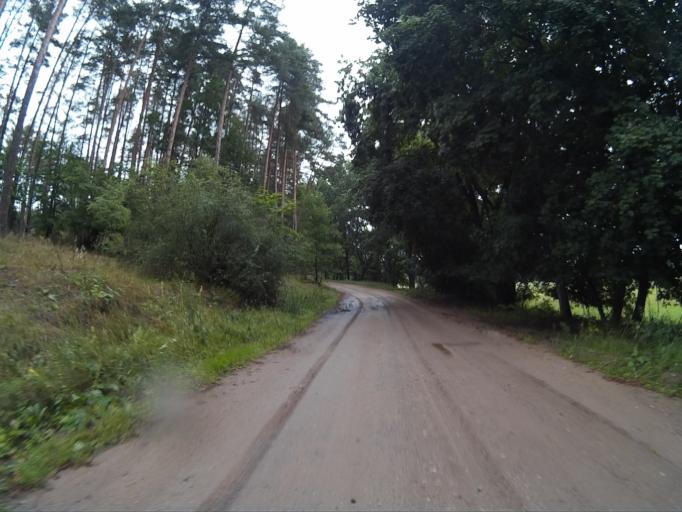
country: PL
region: Kujawsko-Pomorskie
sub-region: Powiat swiecki
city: Osie
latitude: 53.6326
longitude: 18.3736
